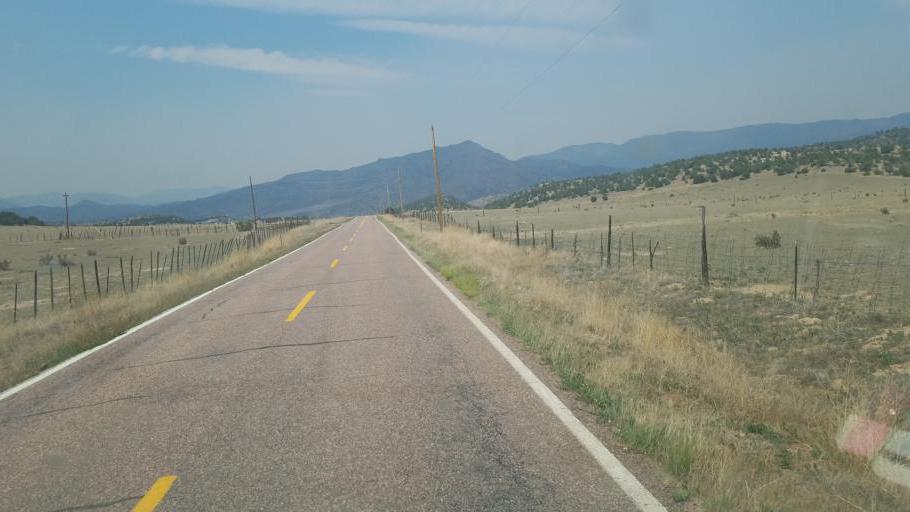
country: US
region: Colorado
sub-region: Fremont County
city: Canon City
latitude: 38.4614
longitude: -105.3762
